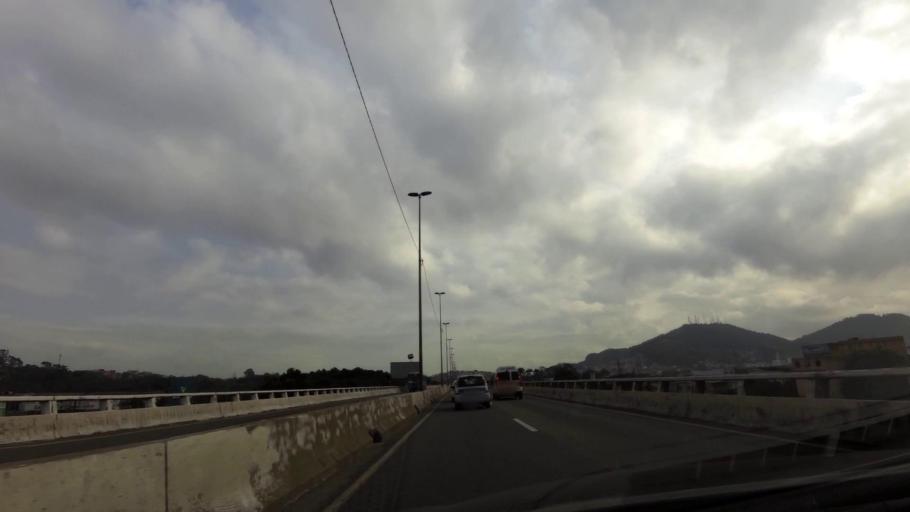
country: BR
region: Espirito Santo
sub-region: Vitoria
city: Vitoria
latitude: -20.3341
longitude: -40.3547
